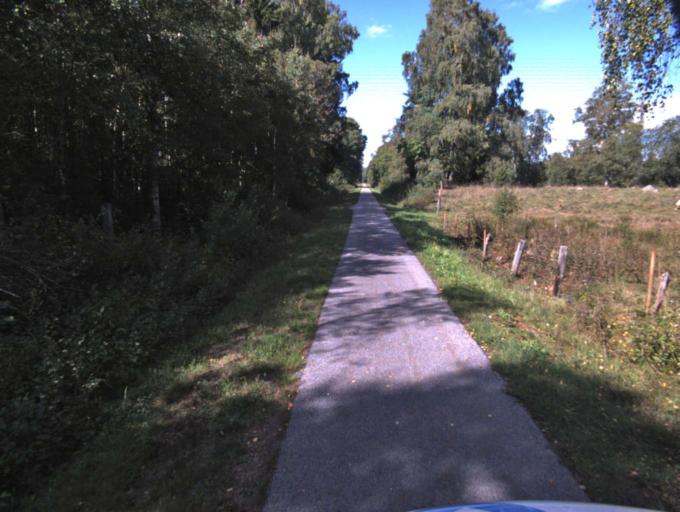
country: SE
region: Vaestra Goetaland
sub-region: Ulricehamns Kommun
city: Ulricehamn
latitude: 57.8314
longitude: 13.3426
